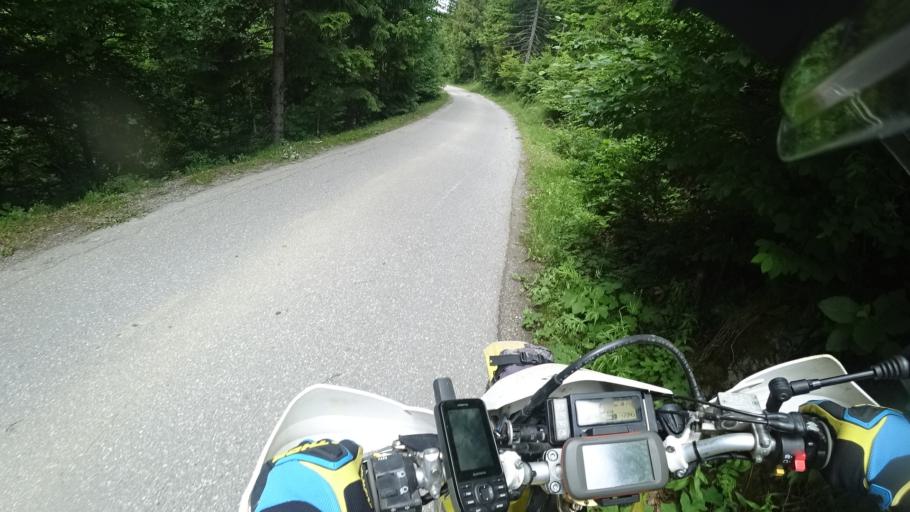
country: SI
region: Loski Potok
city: Hrib-Loski Potok
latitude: 45.6145
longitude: 14.5825
